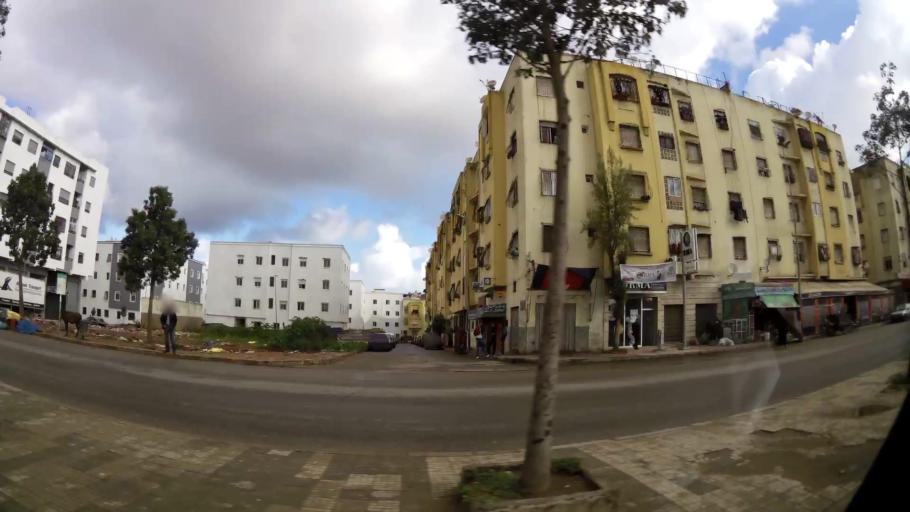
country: MA
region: Grand Casablanca
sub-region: Mediouna
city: Tit Mellil
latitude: 33.5904
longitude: -7.5188
